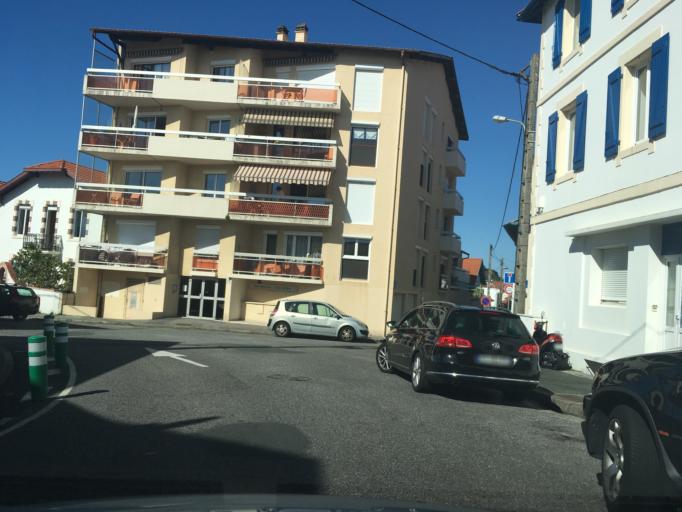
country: FR
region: Aquitaine
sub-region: Departement des Pyrenees-Atlantiques
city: Biarritz
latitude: 43.4754
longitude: -1.5501
